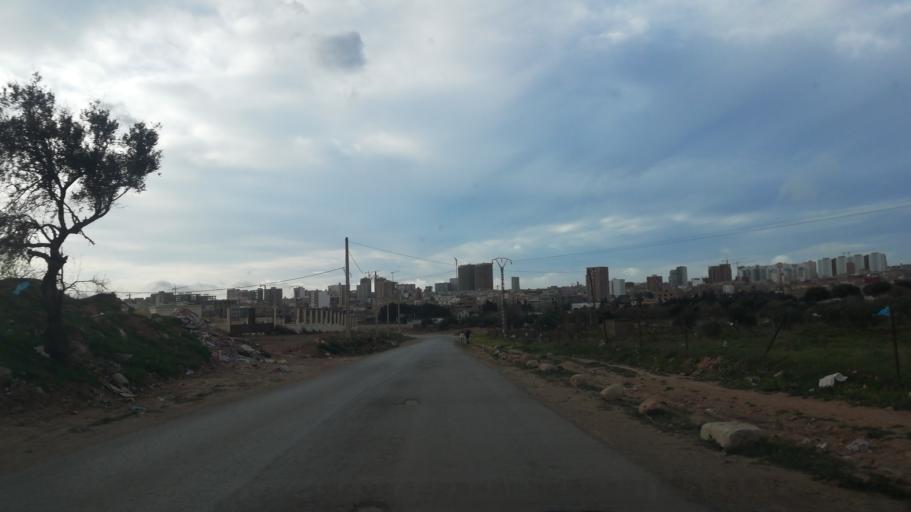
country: DZ
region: Oran
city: Bir el Djir
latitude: 35.7168
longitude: -0.5600
